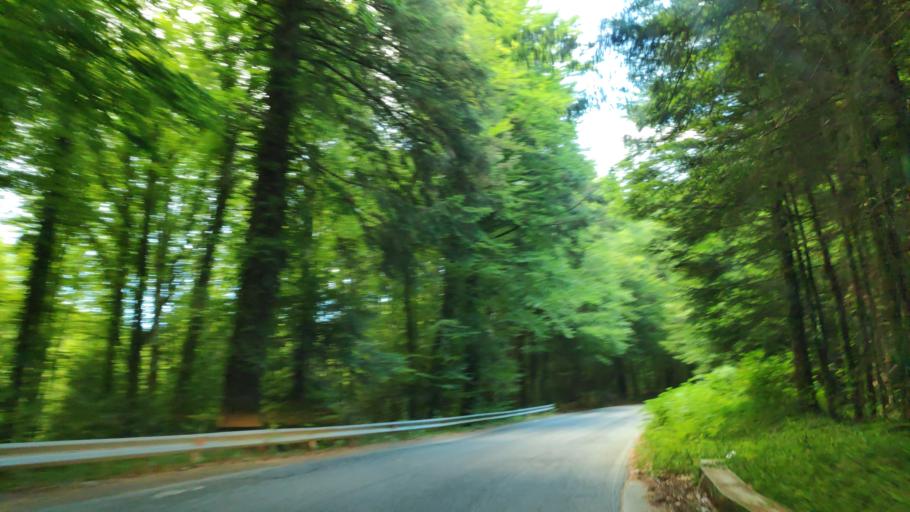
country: IT
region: Calabria
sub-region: Provincia di Vibo-Valentia
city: Serra San Bruno
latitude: 38.5471
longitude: 16.3210
